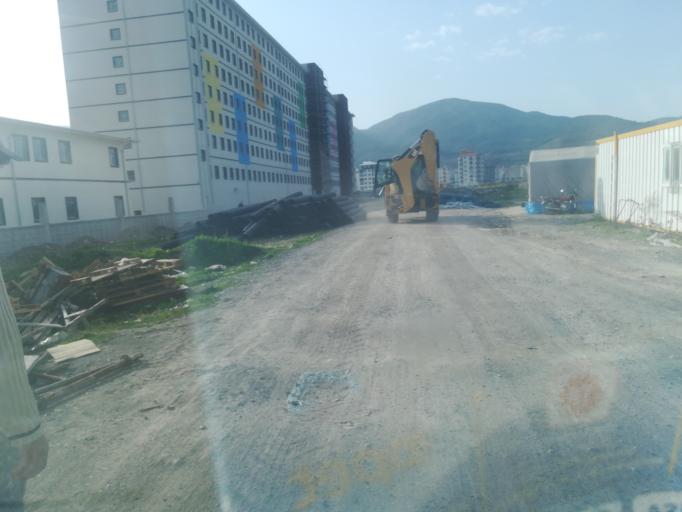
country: TR
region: Osmaniye
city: Osmaniye
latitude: 37.0522
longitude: 36.2312
